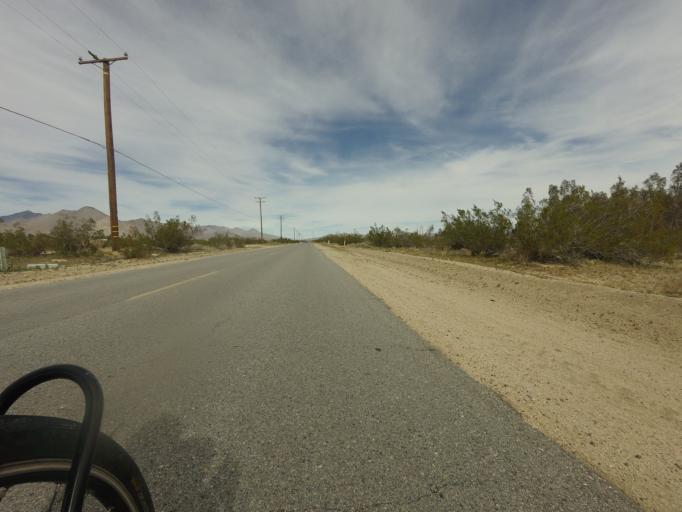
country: US
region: California
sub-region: Kern County
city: Inyokern
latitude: 35.7372
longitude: -117.8391
